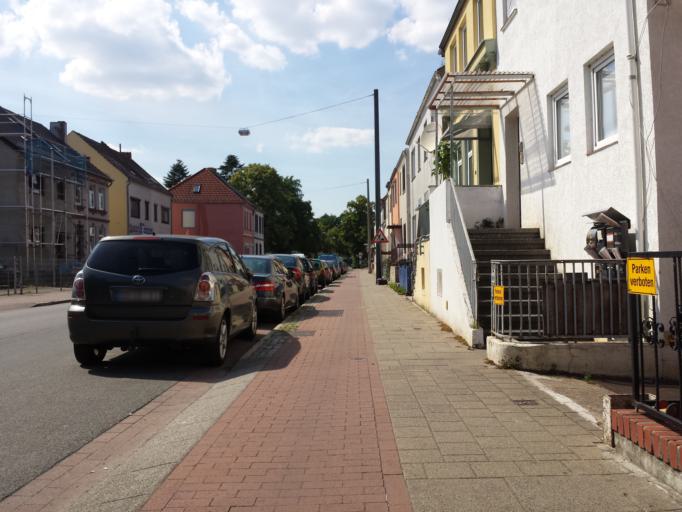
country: DE
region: Bremen
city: Bremen
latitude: 53.0885
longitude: 8.7554
